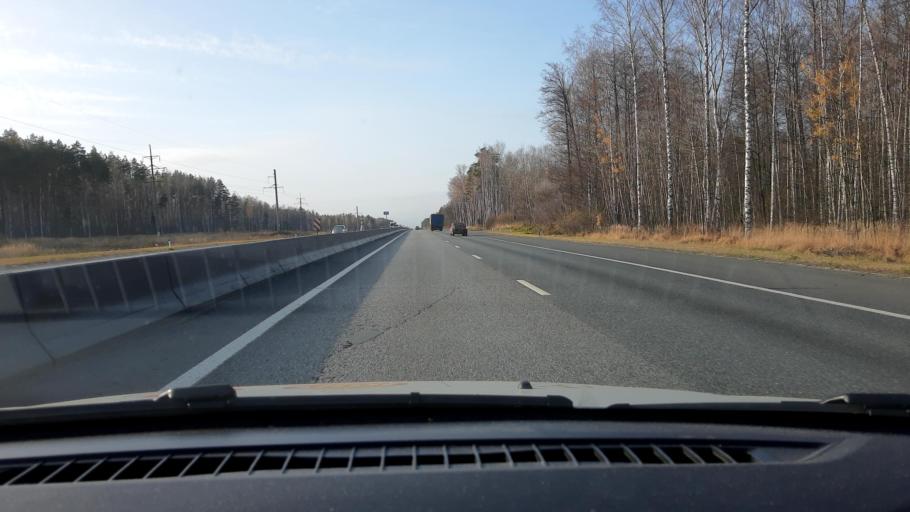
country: RU
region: Nizjnij Novgorod
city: Novosmolinskiy
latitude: 56.2805
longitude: 43.0686
